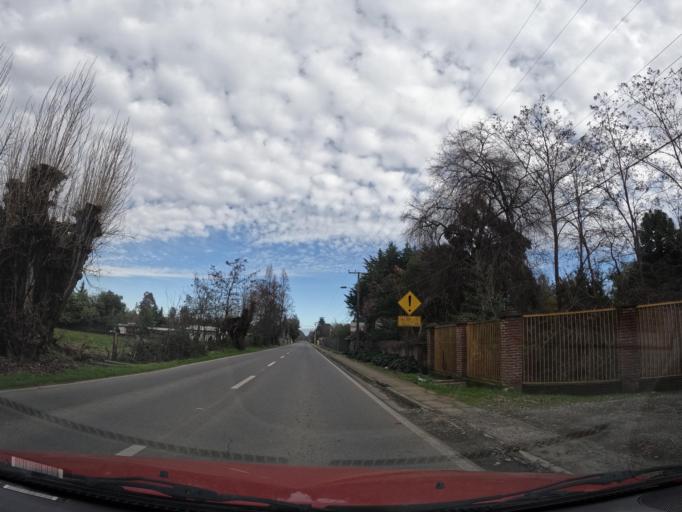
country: CL
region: Maule
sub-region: Provincia de Linares
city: Linares
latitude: -35.8769
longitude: -71.5413
